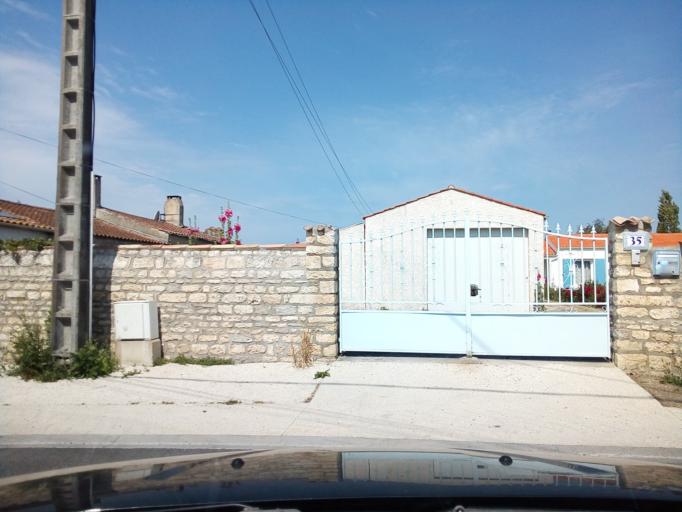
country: FR
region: Poitou-Charentes
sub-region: Departement de la Charente-Maritime
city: Dolus-d'Oleron
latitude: 45.9486
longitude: -1.3021
